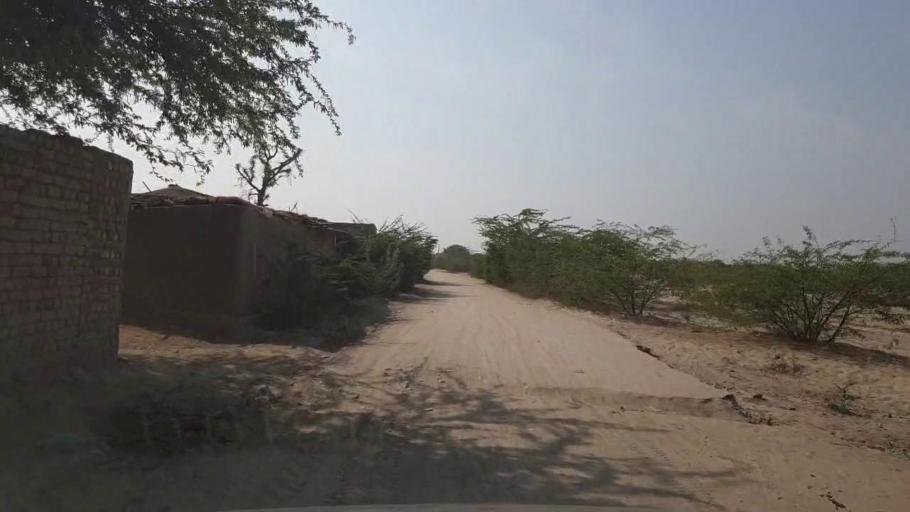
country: PK
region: Sindh
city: Umarkot
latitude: 25.3337
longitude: 69.7349
